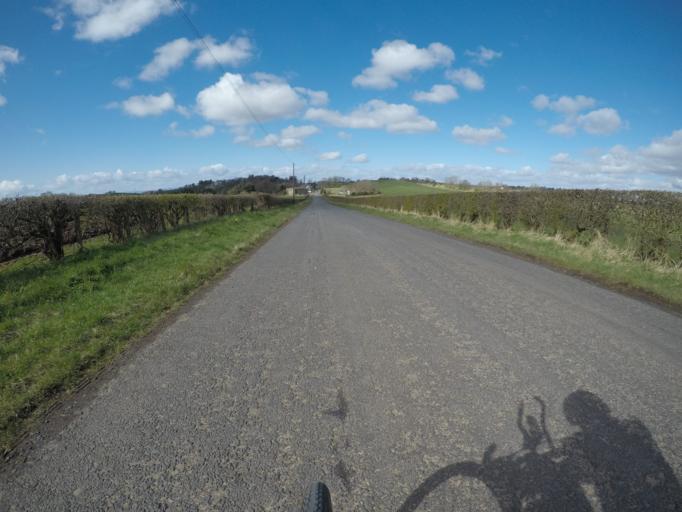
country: GB
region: Scotland
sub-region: East Ayrshire
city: Crosshouse
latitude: 55.6012
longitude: -4.5625
